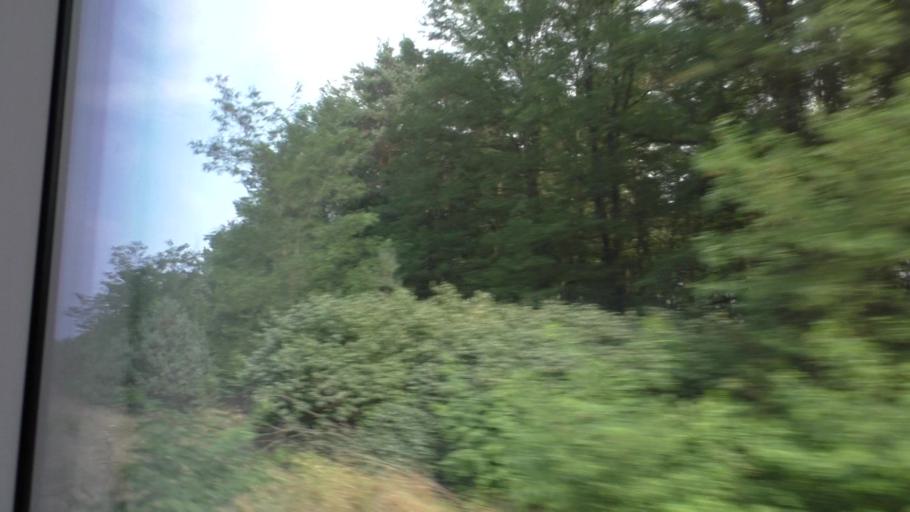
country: DE
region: Brandenburg
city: Mixdorf
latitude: 52.1993
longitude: 14.3958
